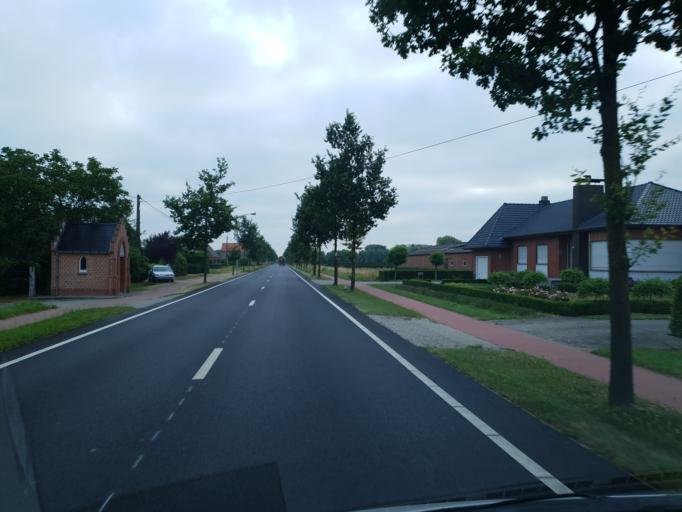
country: BE
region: Flanders
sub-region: Provincie Antwerpen
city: Rijkevorsel
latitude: 51.3704
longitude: 4.7121
